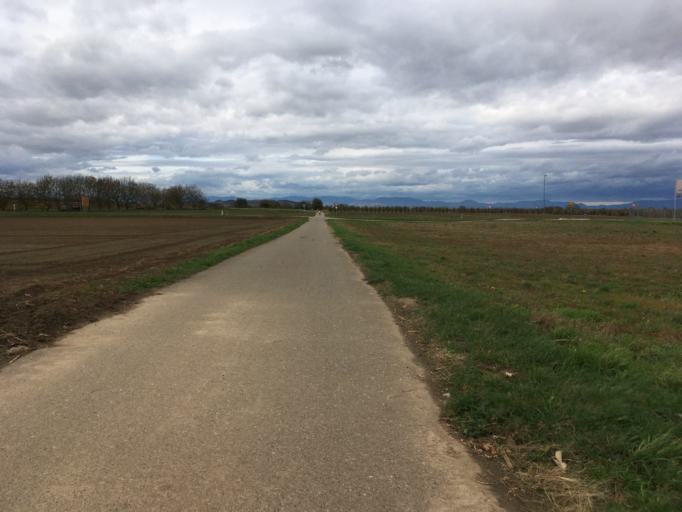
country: DE
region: Baden-Wuerttemberg
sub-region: Freiburg Region
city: Endingen
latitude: 48.1471
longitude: 7.6845
